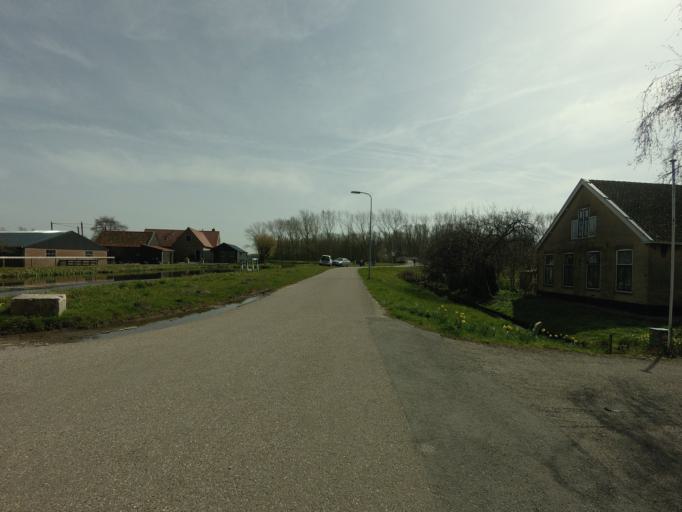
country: NL
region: South Holland
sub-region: Gemeente Den Haag
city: Ypenburg
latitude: 52.0335
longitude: 4.3933
